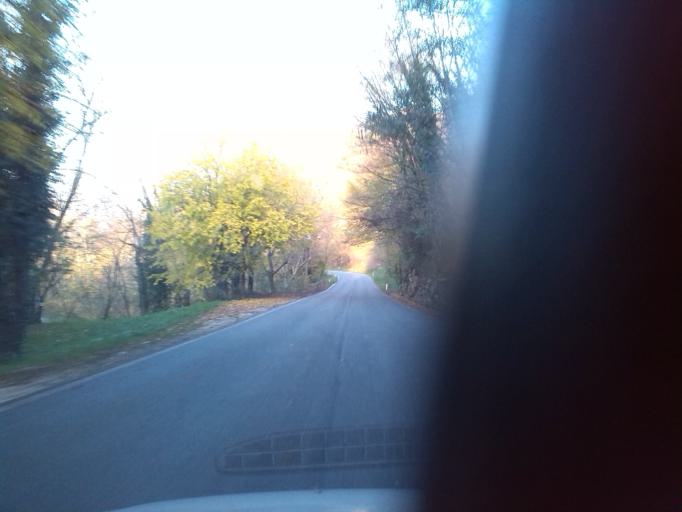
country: IT
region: Friuli Venezia Giulia
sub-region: Provincia di Udine
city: San Pietro al Natisone
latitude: 46.1052
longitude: 13.4720
